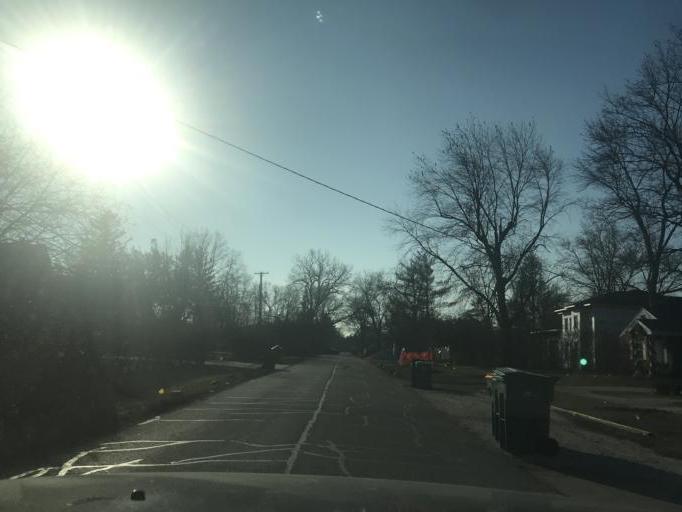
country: US
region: Illinois
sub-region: Cook County
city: Northfield
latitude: 42.0966
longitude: -87.7612
